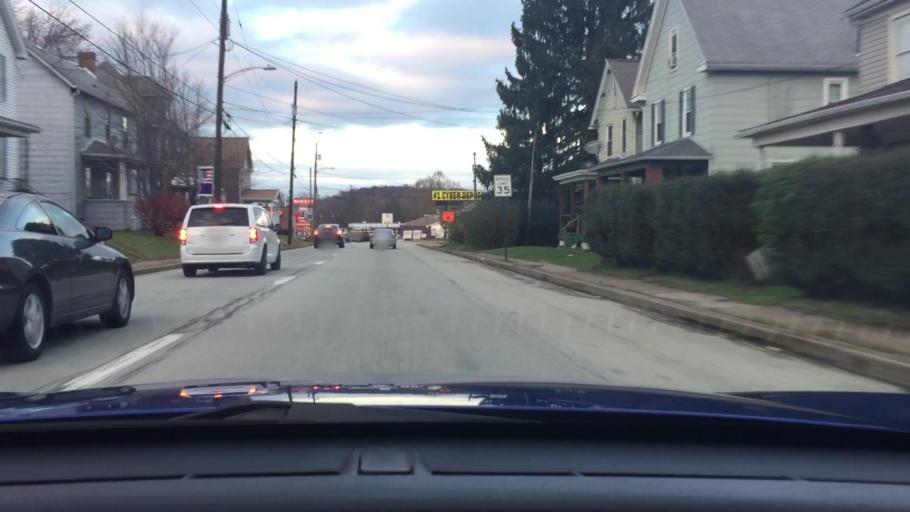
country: US
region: Pennsylvania
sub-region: Westmoreland County
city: Youngwood
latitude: 40.2419
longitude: -79.5765
